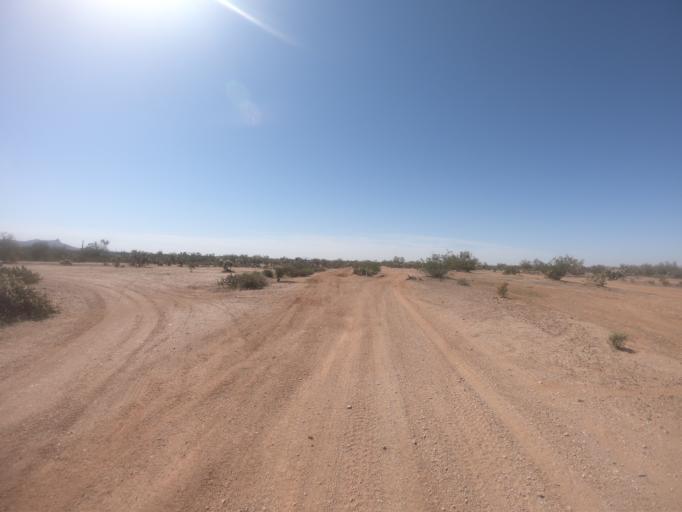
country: US
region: Arizona
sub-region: Pinal County
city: Gold Camp
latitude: 33.2507
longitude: -111.3053
